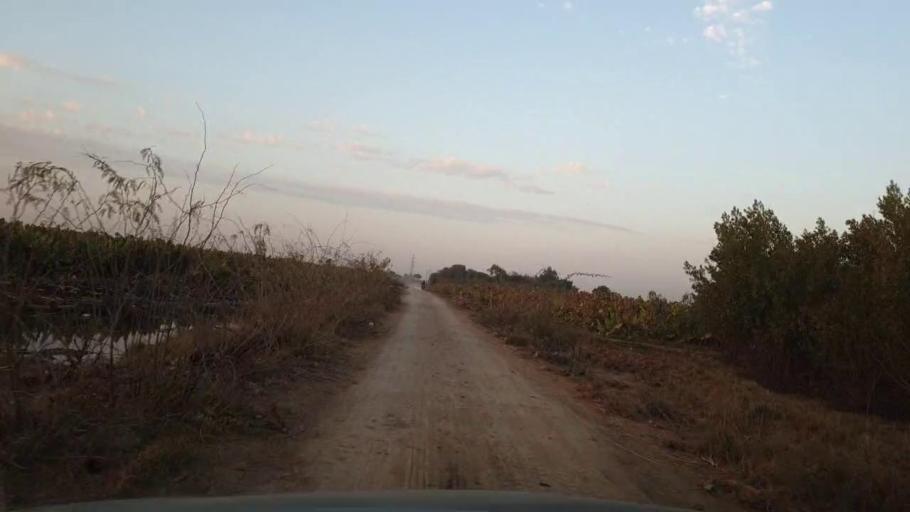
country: PK
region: Sindh
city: Matiari
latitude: 25.6115
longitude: 68.4831
